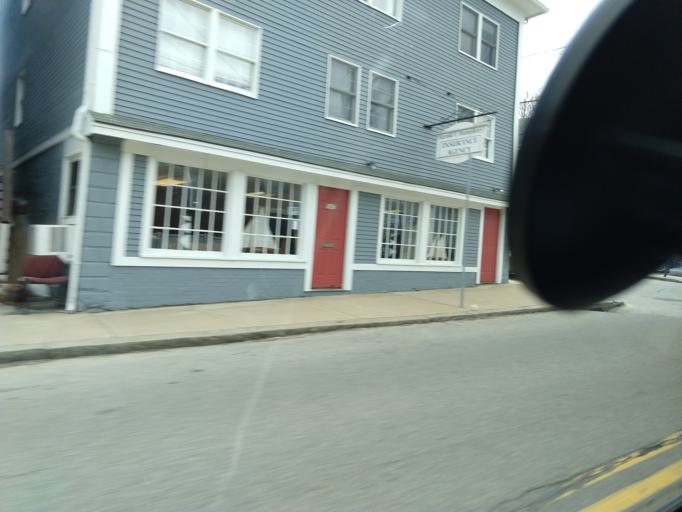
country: US
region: Massachusetts
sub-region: Essex County
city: Newburyport
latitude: 42.8138
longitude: -70.8768
